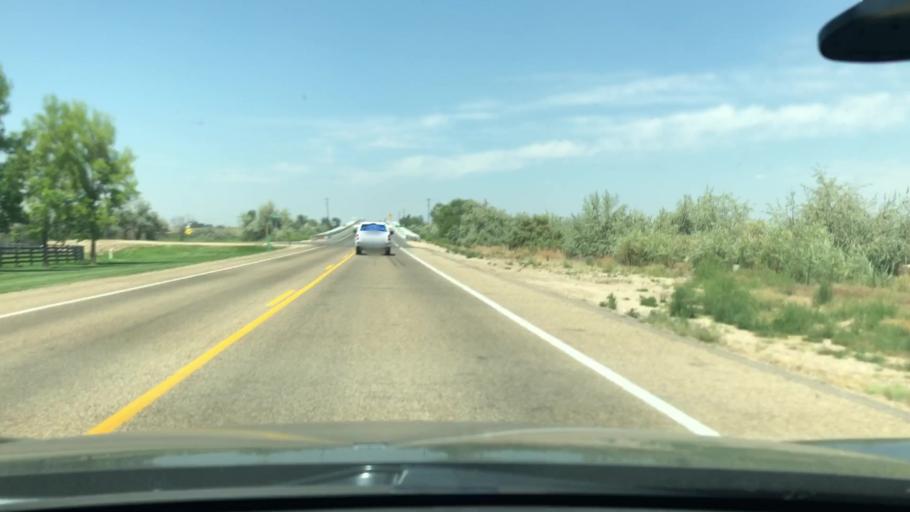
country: US
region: Idaho
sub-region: Canyon County
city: Parma
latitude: 43.7617
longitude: -116.9117
